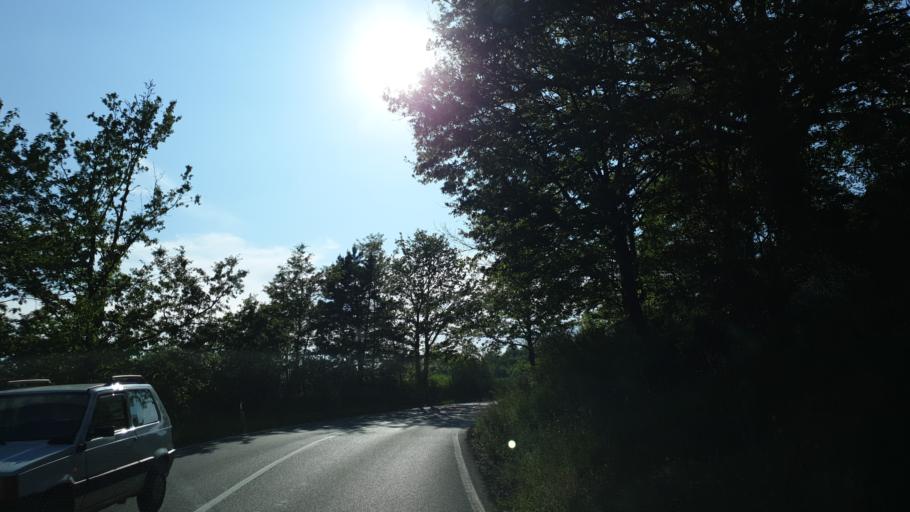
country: IT
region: Tuscany
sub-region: Province of Arezzo
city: Stia
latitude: 43.7809
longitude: 11.6659
